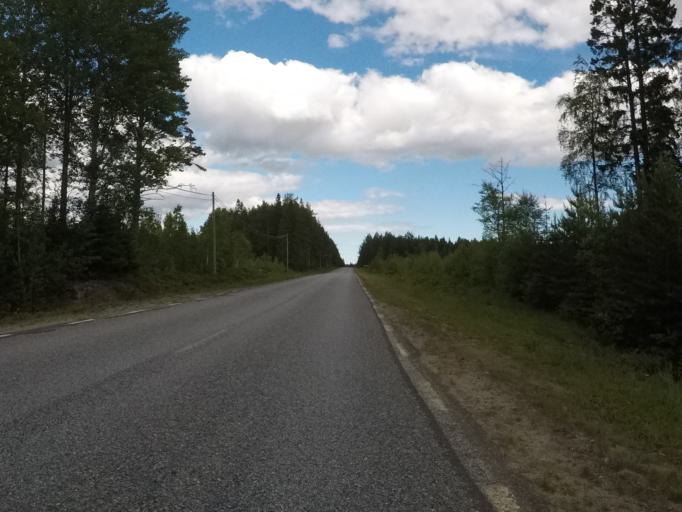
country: SE
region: Vaesterbotten
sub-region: Umea Kommun
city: Saevar
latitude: 63.9232
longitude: 20.7698
